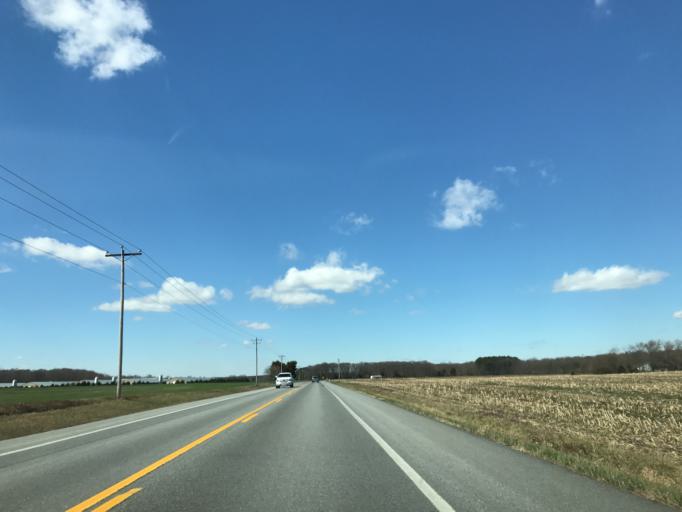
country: US
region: Maryland
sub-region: Caroline County
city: Ridgely
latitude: 39.1010
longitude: -75.8909
